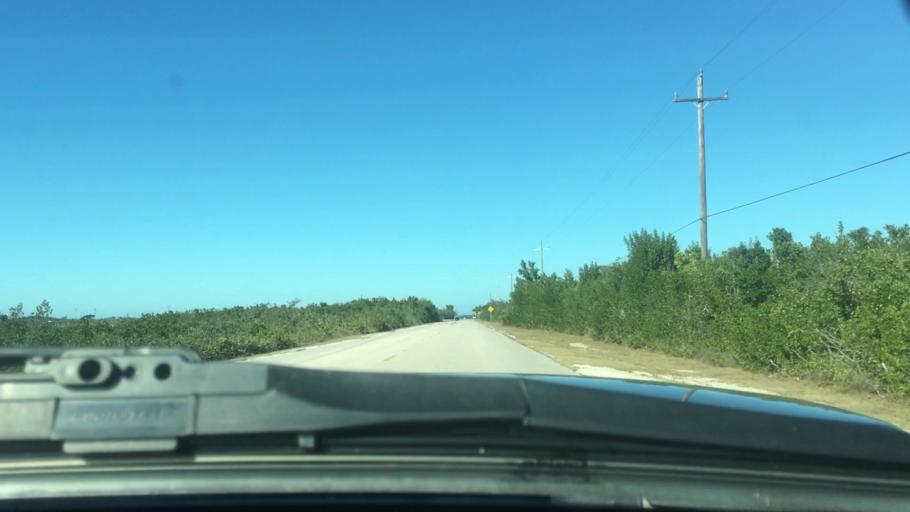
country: US
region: Florida
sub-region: Monroe County
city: Cudjoe Key
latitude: 24.6896
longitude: -81.4996
